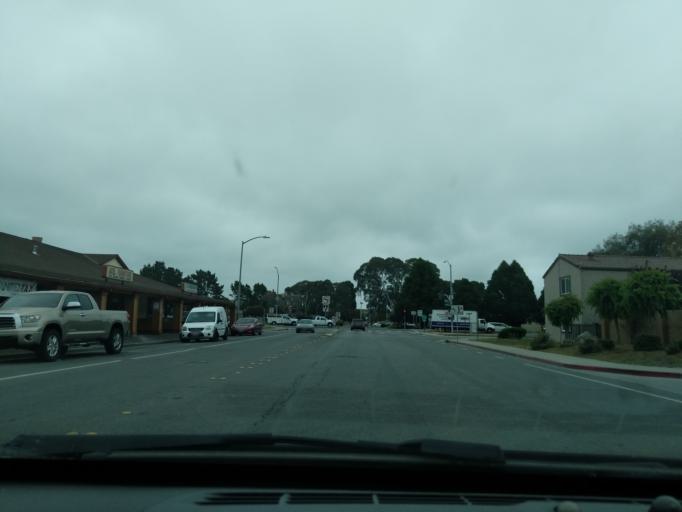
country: US
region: California
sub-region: Santa Cruz County
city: Watsonville
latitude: 36.9174
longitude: -121.7715
